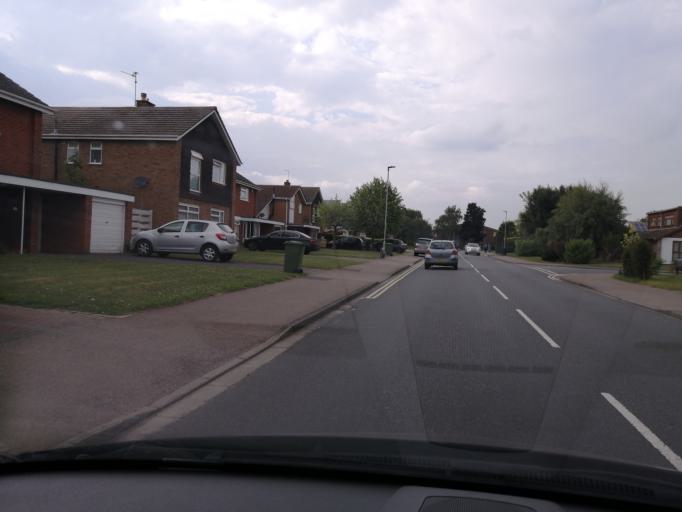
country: GB
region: England
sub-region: Peterborough
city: Peterborough
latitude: 52.5781
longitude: -0.2743
